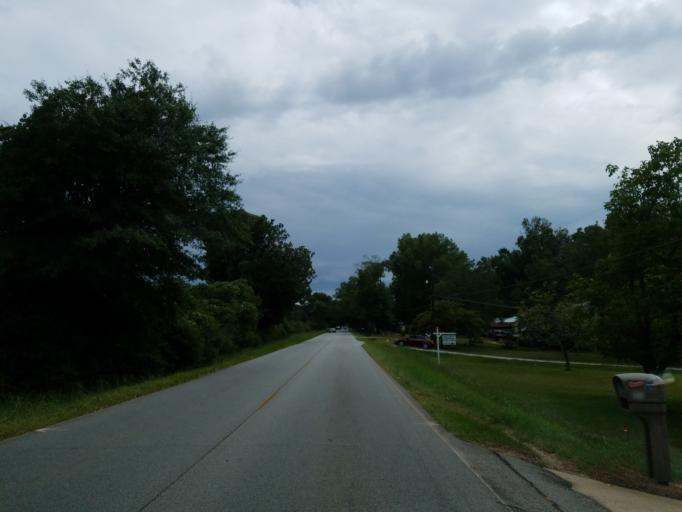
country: US
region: Georgia
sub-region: Spalding County
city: Experiment
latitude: 33.2875
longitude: -84.2850
